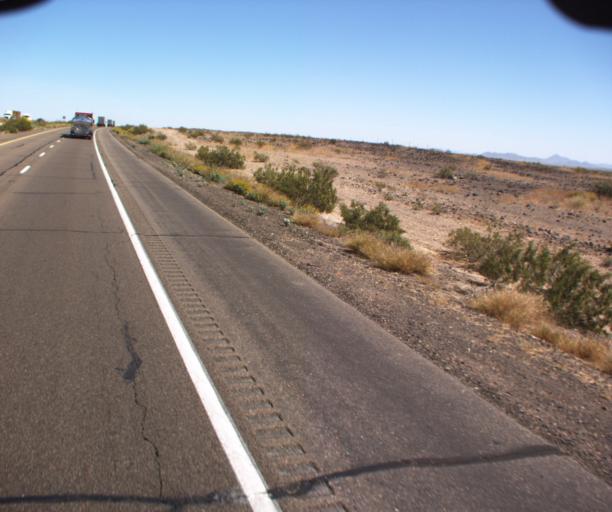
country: US
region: Arizona
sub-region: Maricopa County
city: Gila Bend
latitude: 32.8892
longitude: -113.0704
